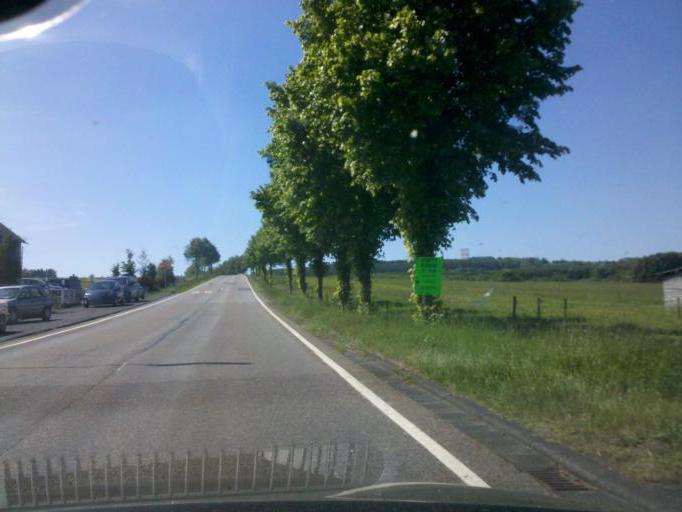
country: DE
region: Rheinland-Pfalz
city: Bretthausen
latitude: 50.6586
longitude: 8.0722
